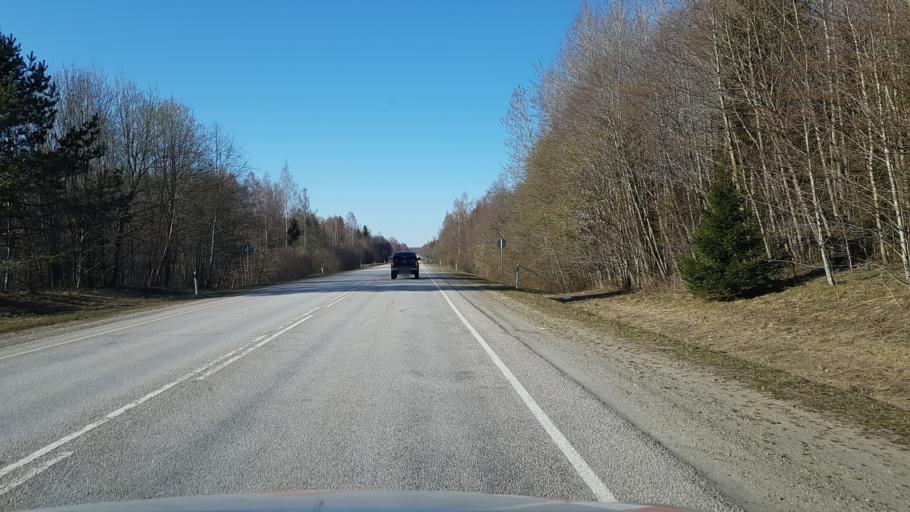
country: EE
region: Ida-Virumaa
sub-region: Johvi vald
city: Johvi
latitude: 59.1679
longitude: 27.3519
